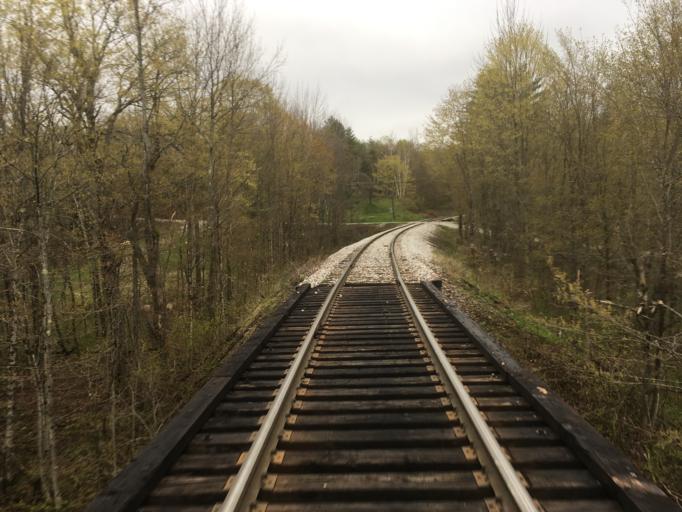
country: US
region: Vermont
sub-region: Rutland County
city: Rutland
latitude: 43.4758
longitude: -72.8722
